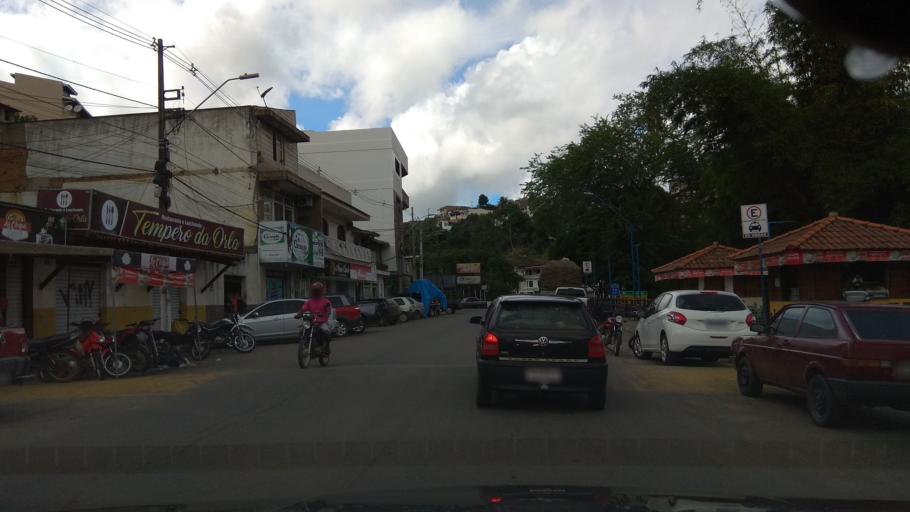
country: BR
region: Bahia
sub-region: Mutuipe
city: Mutuipe
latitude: -13.2268
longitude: -39.5034
